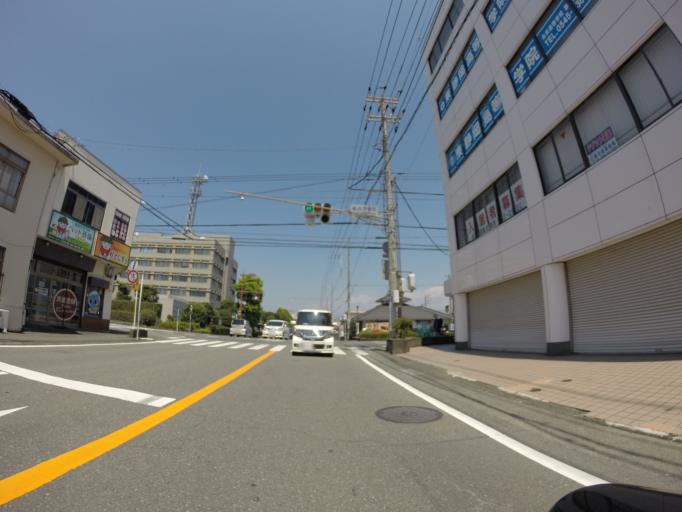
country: JP
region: Shizuoka
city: Fuji
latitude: 35.1558
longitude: 138.6624
